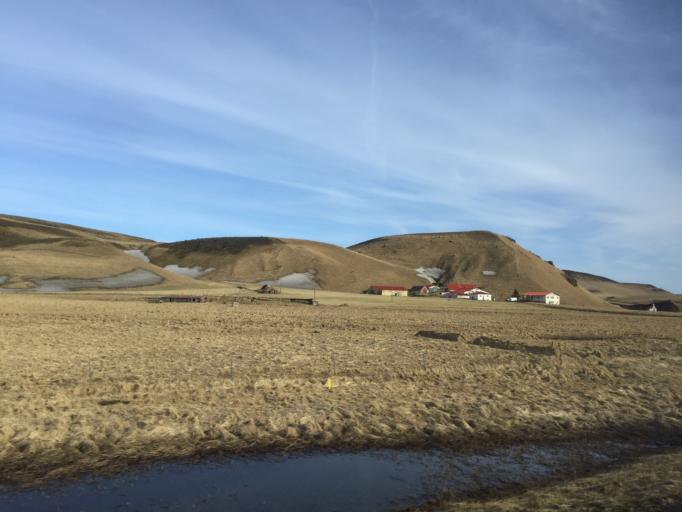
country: IS
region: South
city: Vestmannaeyjar
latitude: 63.4391
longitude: -19.1960
